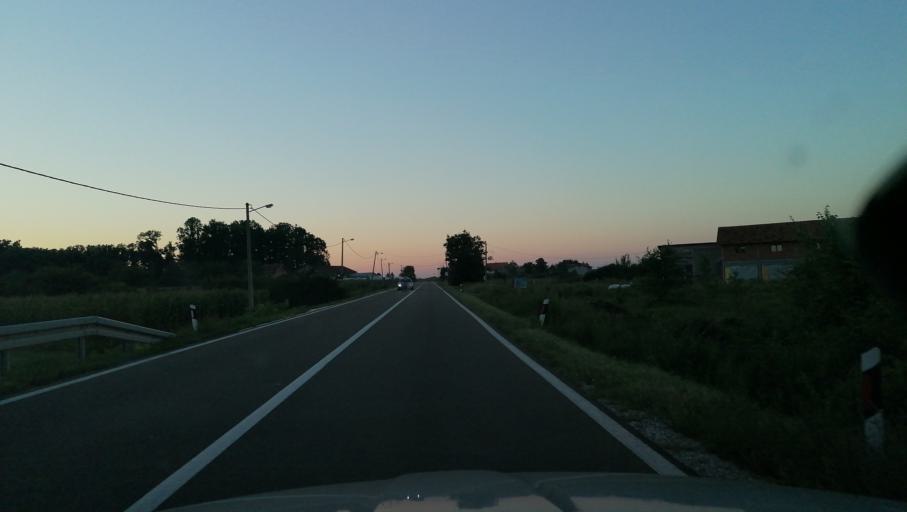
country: RS
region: Central Serbia
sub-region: Sumadijski Okrug
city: Topola
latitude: 44.3358
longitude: 20.6858
